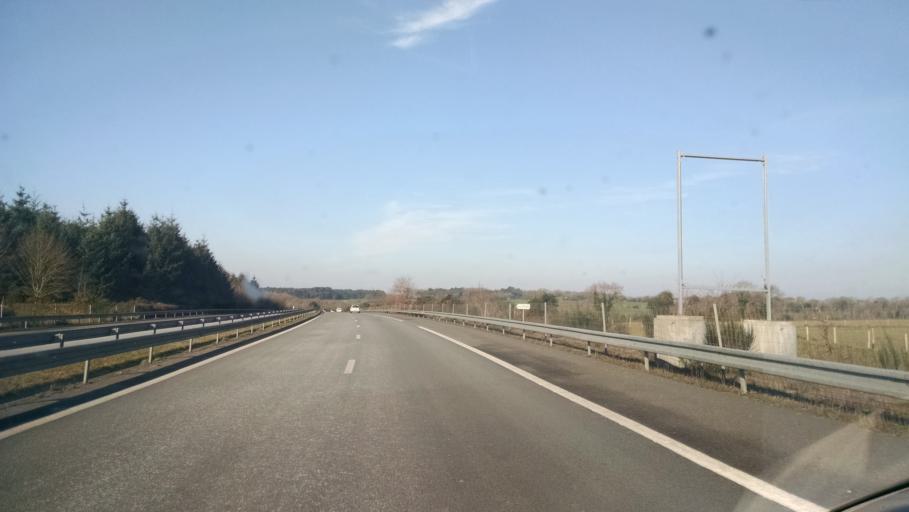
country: FR
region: Brittany
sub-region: Departement du Morbihan
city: Ambon
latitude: 47.5921
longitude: -2.5581
